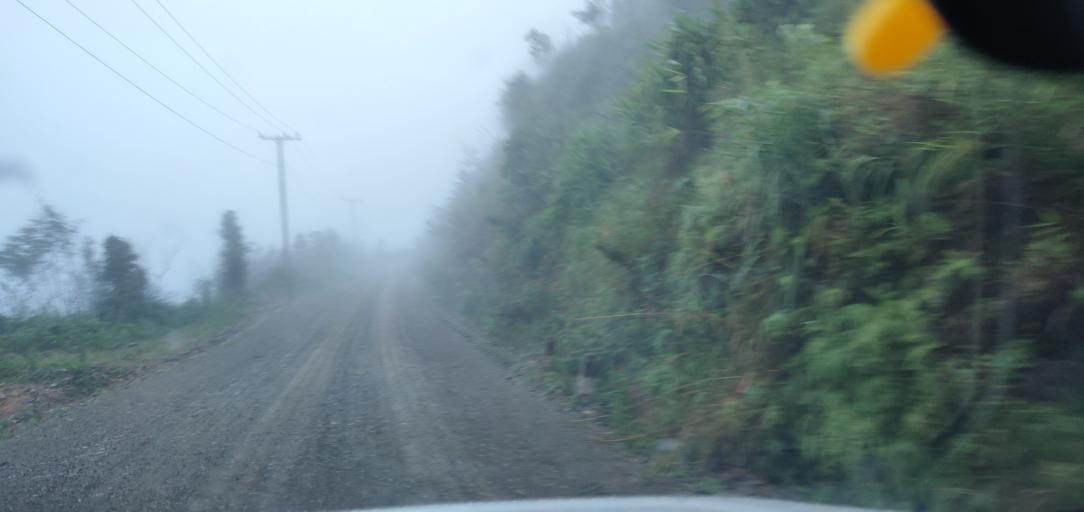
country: LA
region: Phongsali
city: Phongsali
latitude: 21.3938
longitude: 102.2059
